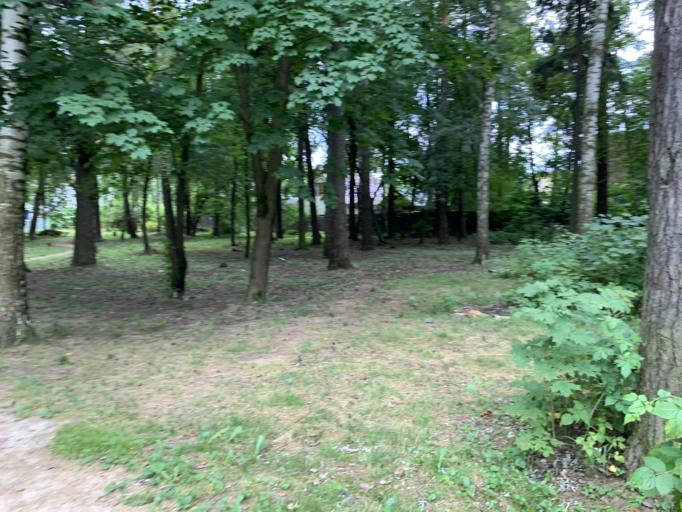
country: RU
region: Moskovskaya
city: Mamontovka
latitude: 55.9919
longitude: 37.8100
